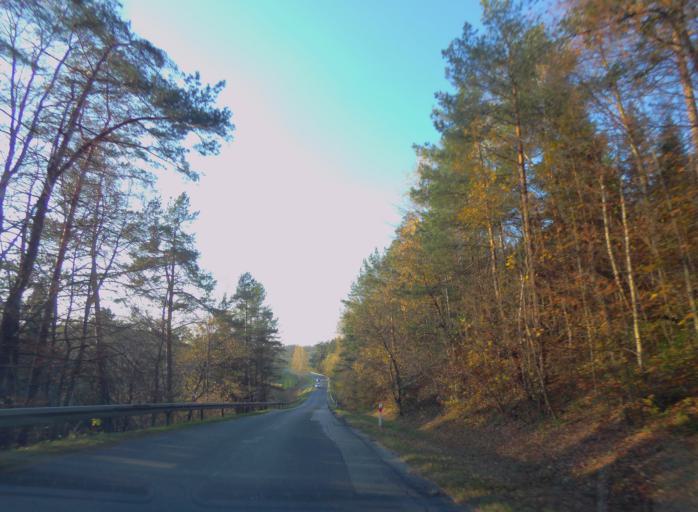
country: PL
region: Subcarpathian Voivodeship
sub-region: Powiat leski
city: Polanczyk
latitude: 49.3874
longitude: 22.4009
